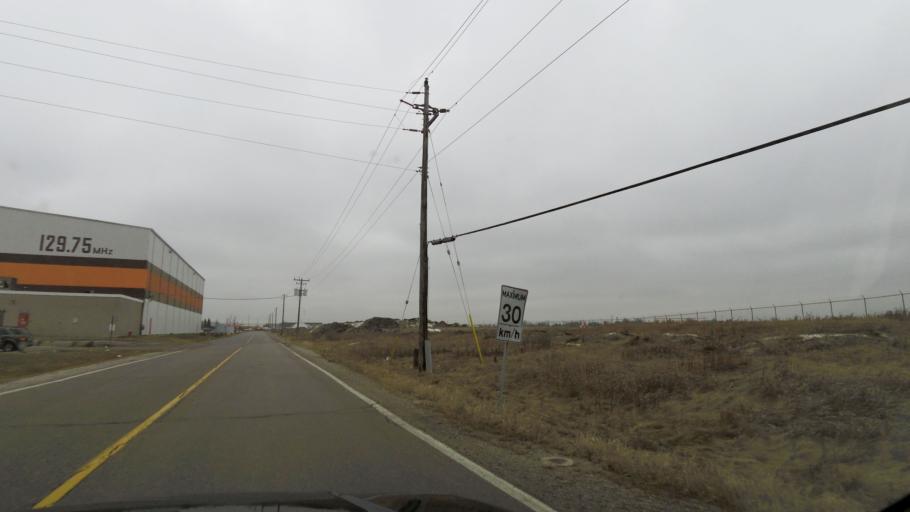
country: CA
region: Ontario
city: Etobicoke
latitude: 43.6929
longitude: -79.6483
